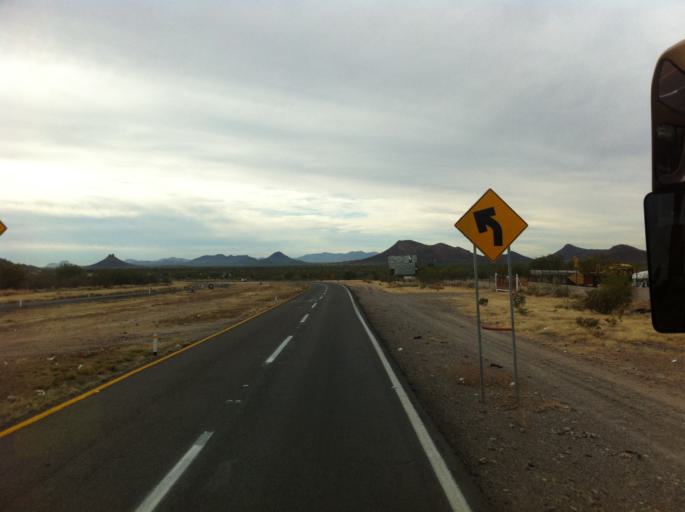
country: MX
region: Sonora
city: Hermosillo
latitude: 28.9462
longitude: -110.9624
